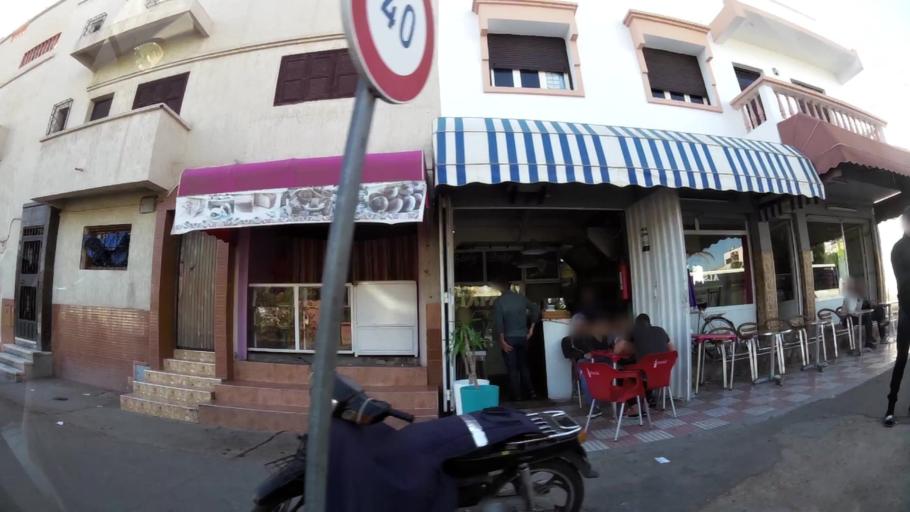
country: MA
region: Souss-Massa-Draa
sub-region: Agadir-Ida-ou-Tnan
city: Agadir
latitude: 30.4289
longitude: -9.5830
